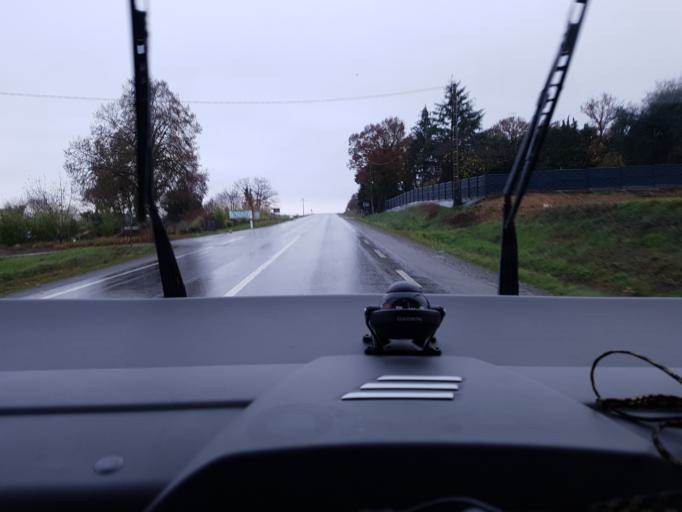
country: FR
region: Brittany
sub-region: Departement d'Ille-et-Vilaine
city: Etrelles
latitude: 48.0860
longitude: -1.2031
